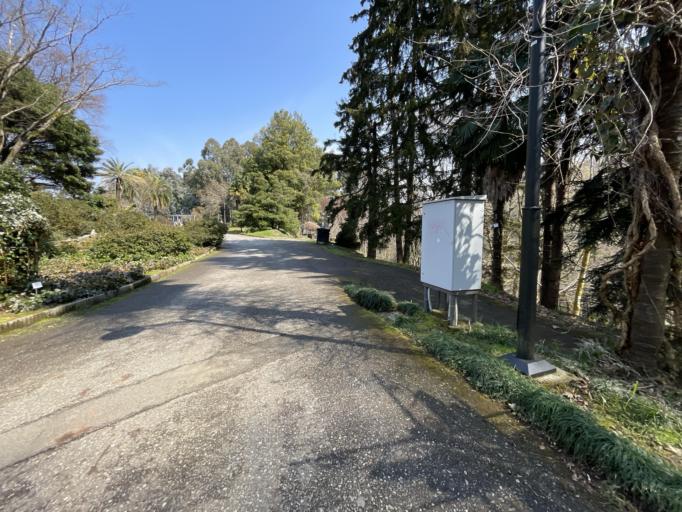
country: GE
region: Ajaria
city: Makhinjauri
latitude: 41.6978
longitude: 41.7165
